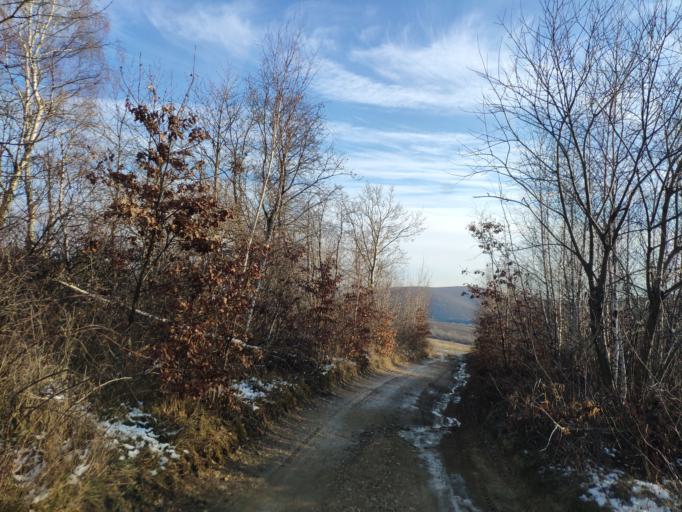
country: SK
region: Kosicky
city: Moldava nad Bodvou
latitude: 48.7358
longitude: 21.0920
